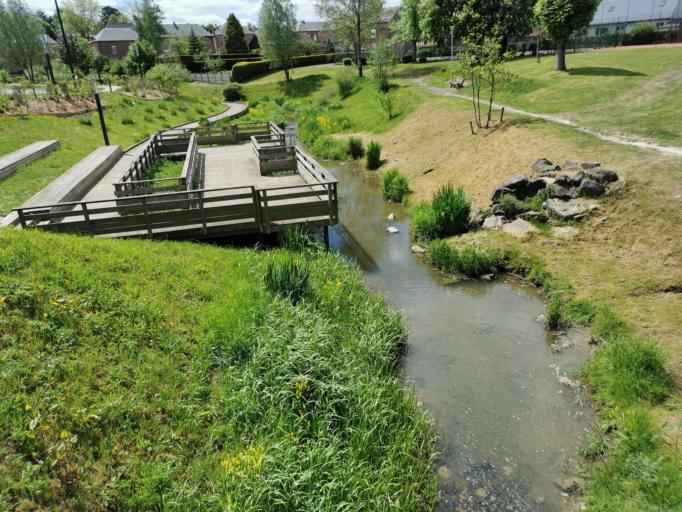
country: FR
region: Nord-Pas-de-Calais
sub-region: Departement du Nord
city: Anor
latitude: 49.9917
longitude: 4.0977
